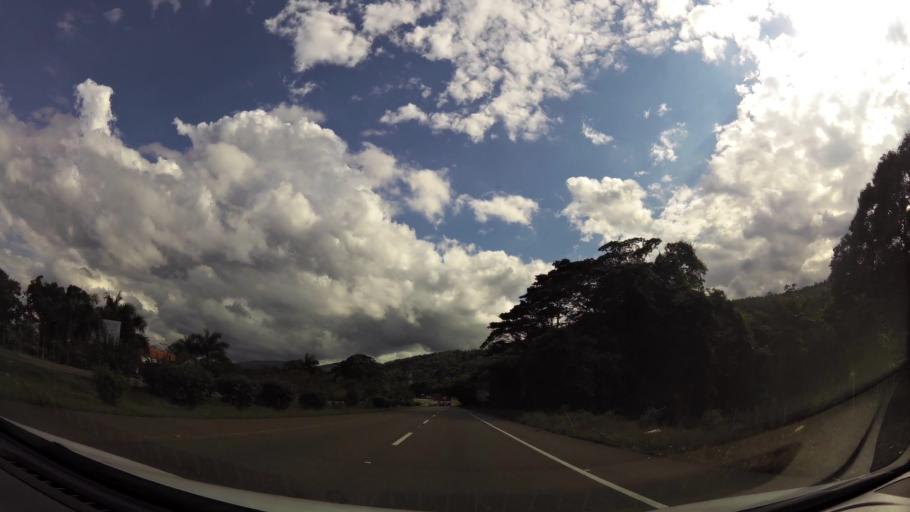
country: DO
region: La Vega
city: Concepcion de La Vega
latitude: 19.1879
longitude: -70.4985
